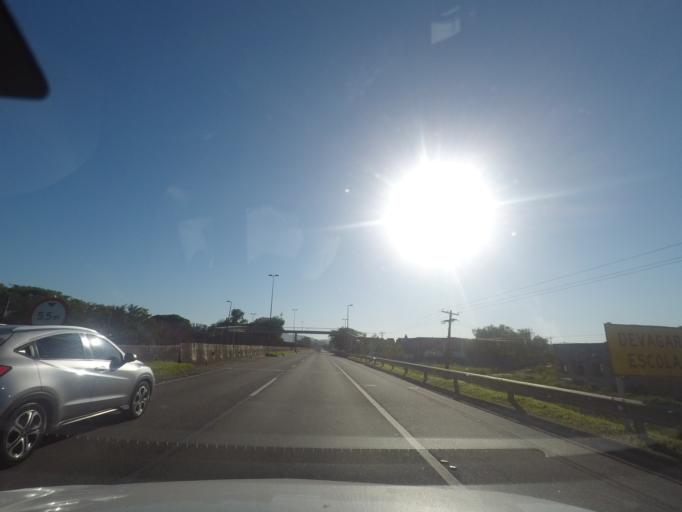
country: BR
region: Rio de Janeiro
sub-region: Petropolis
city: Petropolis
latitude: -22.6467
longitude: -43.2128
